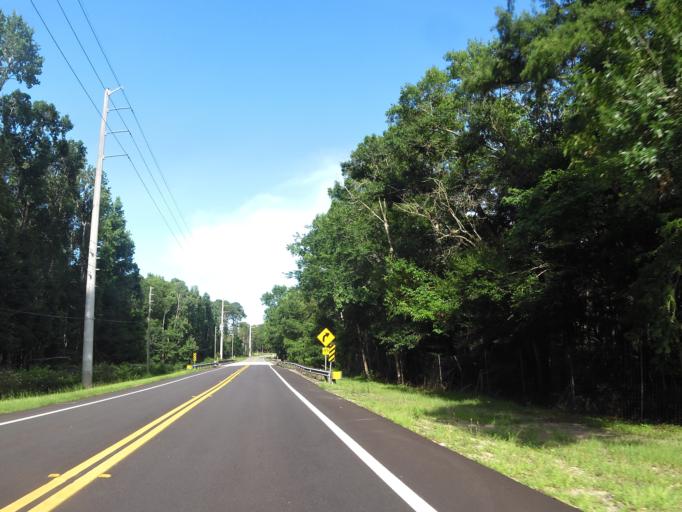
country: US
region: Florida
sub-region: Clay County
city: Green Cove Springs
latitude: 30.0149
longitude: -81.5650
